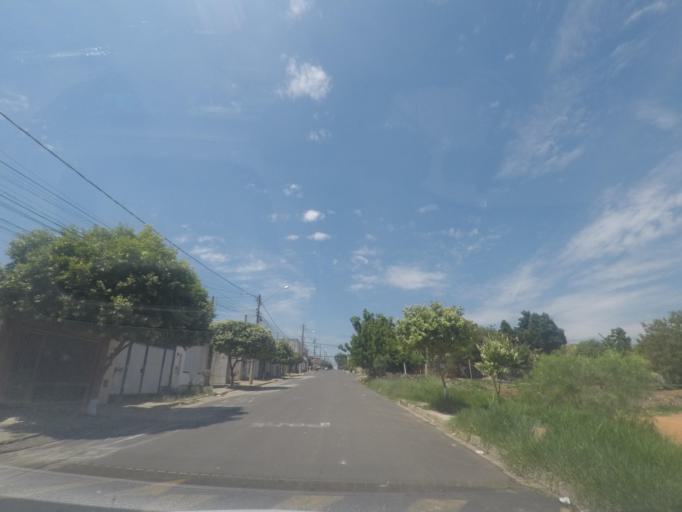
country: BR
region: Sao Paulo
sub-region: Sumare
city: Sumare
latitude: -22.7978
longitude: -47.2677
